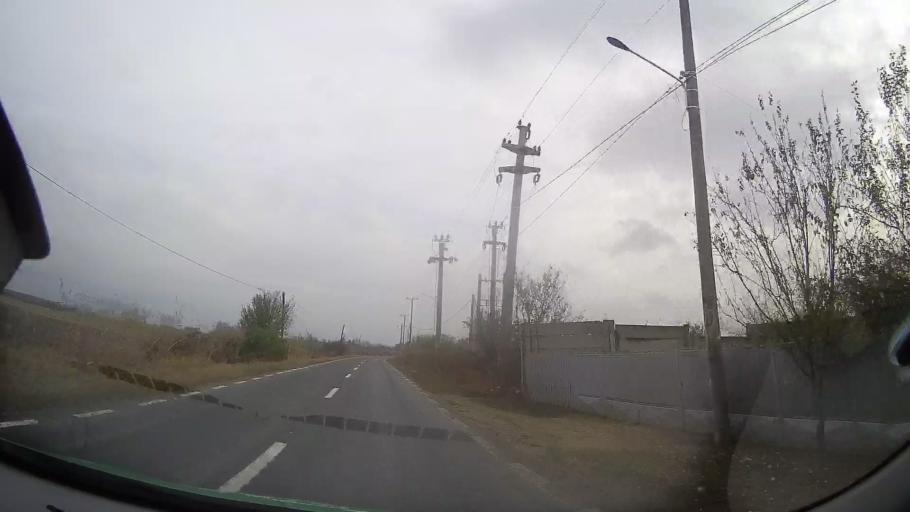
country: RO
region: Ilfov
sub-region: Comuna Gruiu
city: Lipia
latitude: 44.7196
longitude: 26.2705
